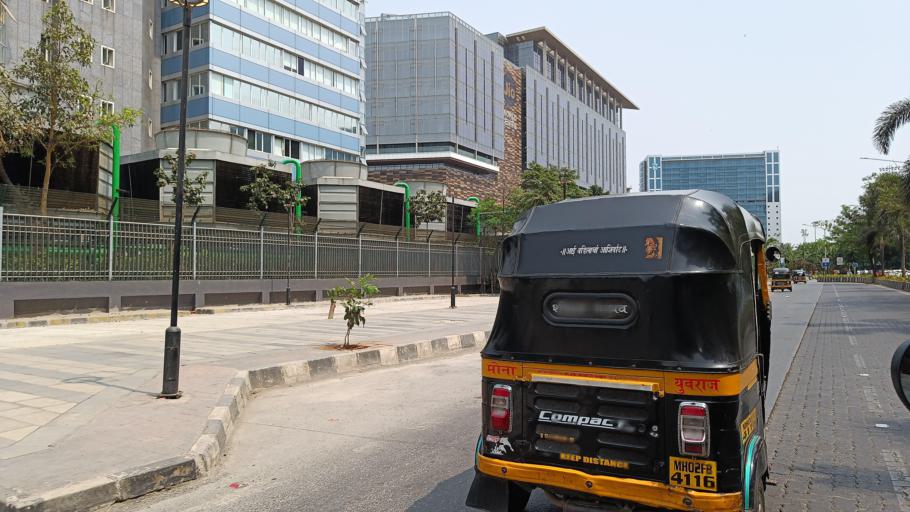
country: IN
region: Maharashtra
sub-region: Mumbai Suburban
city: Mumbai
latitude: 19.0635
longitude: 72.8642
